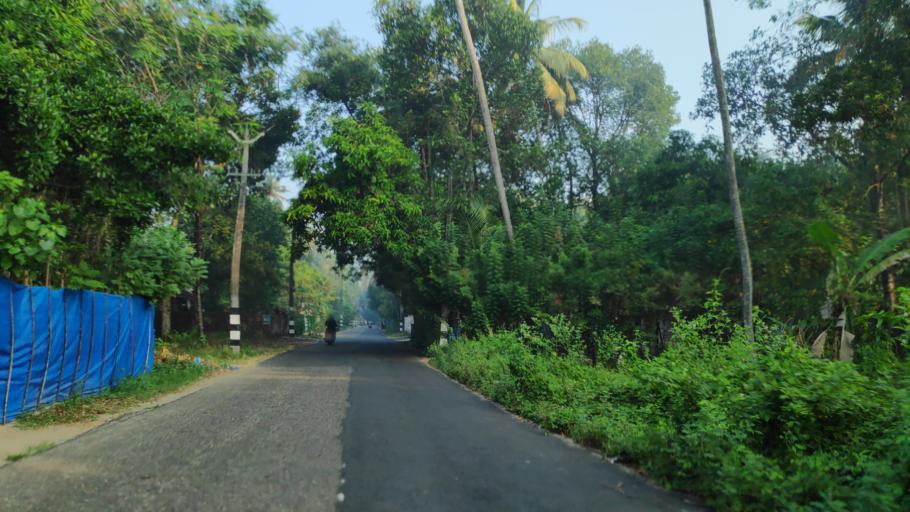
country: IN
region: Kerala
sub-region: Alappuzha
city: Vayalar
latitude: 9.6965
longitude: 76.2902
